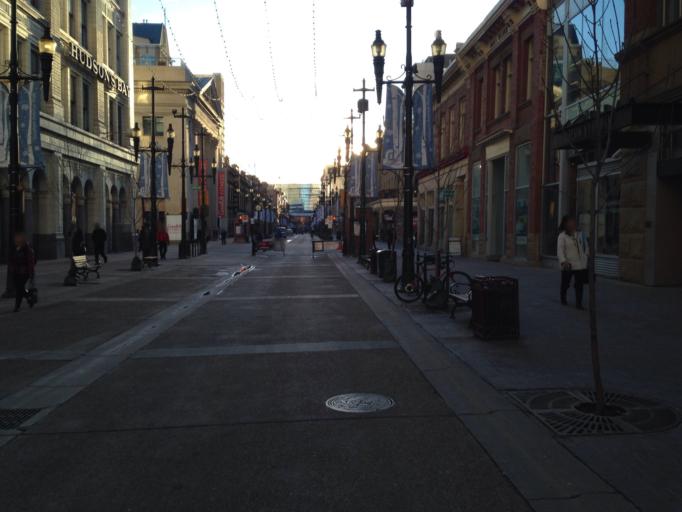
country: CA
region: Alberta
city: Calgary
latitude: 51.0456
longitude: -114.0665
